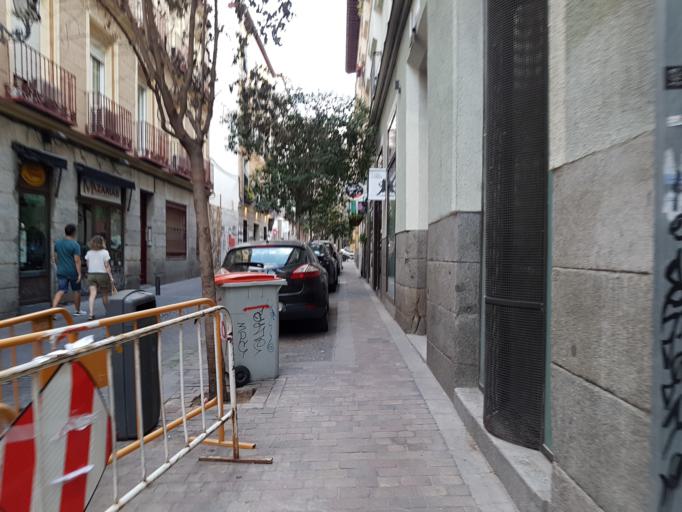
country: ES
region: Madrid
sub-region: Provincia de Madrid
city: Madrid
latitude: 40.4116
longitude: -3.6948
